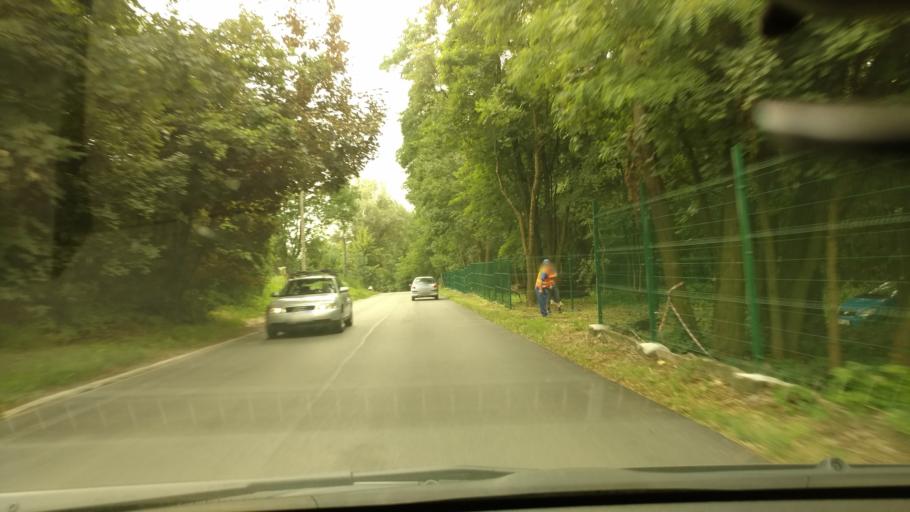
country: PL
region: Lesser Poland Voivodeship
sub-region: Powiat krakowski
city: Zielonki
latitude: 50.1115
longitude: 19.9431
